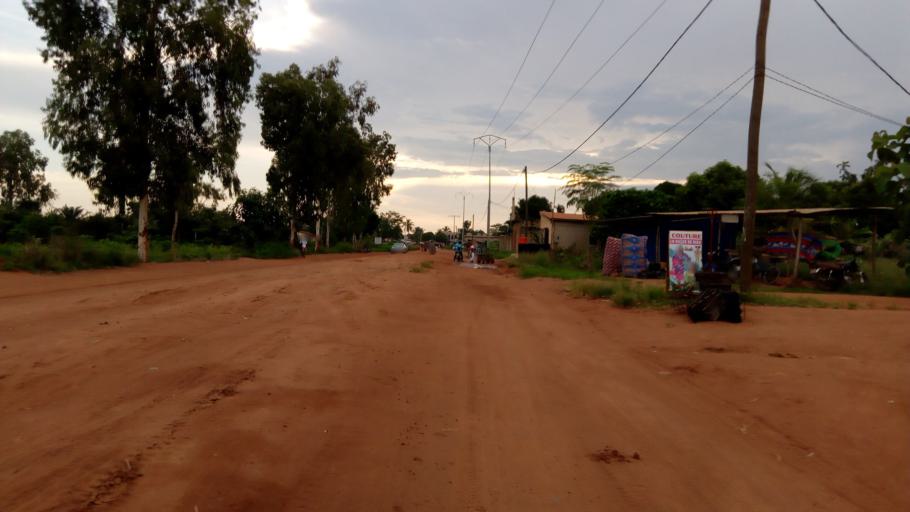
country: TG
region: Maritime
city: Lome
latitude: 6.2623
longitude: 1.1410
